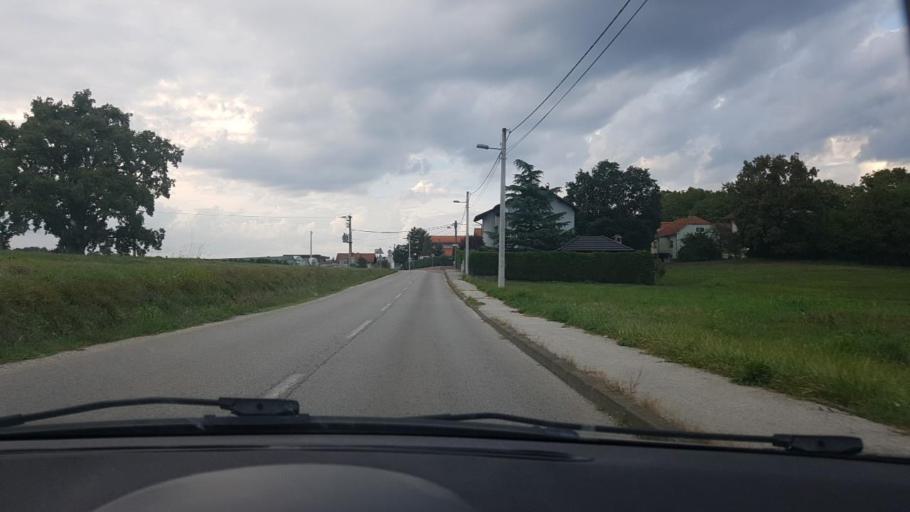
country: HR
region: Grad Zagreb
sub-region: Sesvete
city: Sesvete
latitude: 45.8970
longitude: 16.1667
